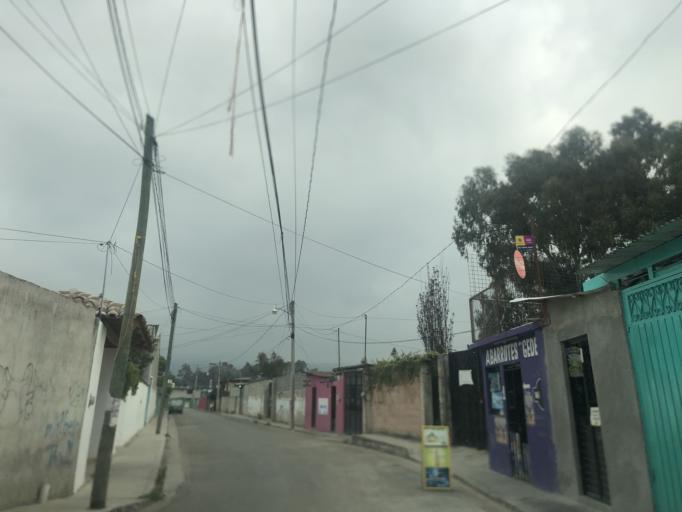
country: MX
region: Chiapas
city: San Cristobal de las Casas
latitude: 16.7175
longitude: -92.6418
